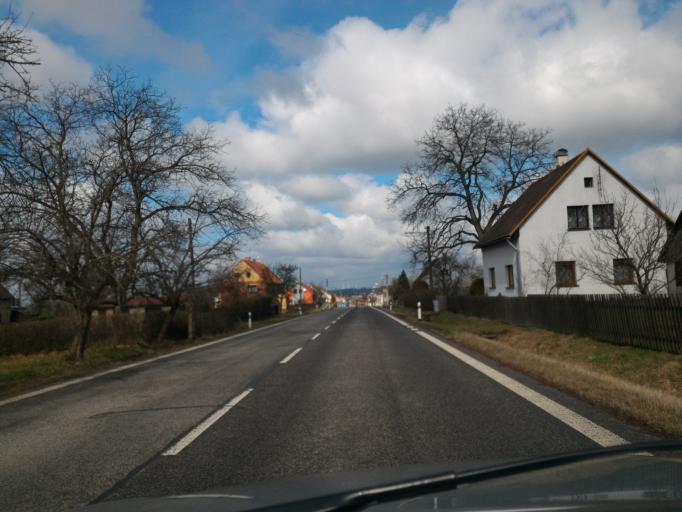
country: PL
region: Silesian Voivodeship
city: Zawidow
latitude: 51.0124
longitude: 15.0677
